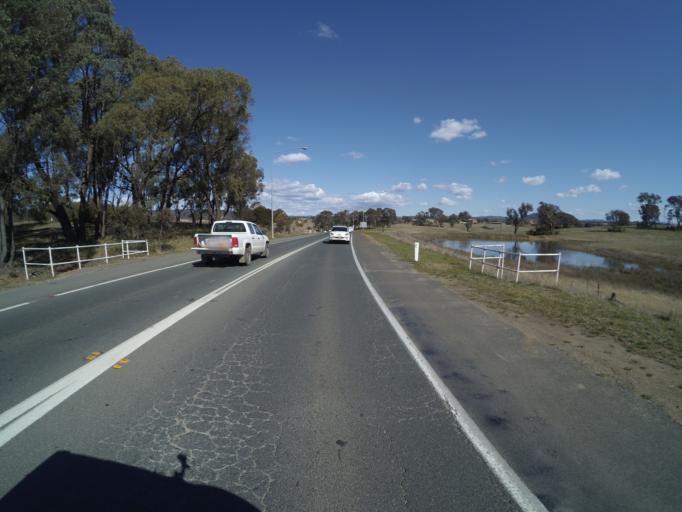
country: AU
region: New South Wales
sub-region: Queanbeyan
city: Queanbeyan
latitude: -35.3323
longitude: 149.2384
